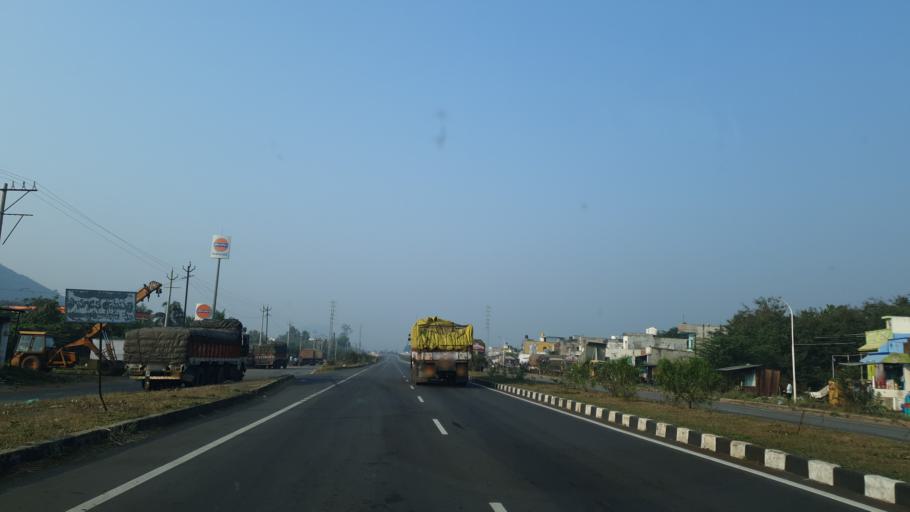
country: IN
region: Andhra Pradesh
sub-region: Srikakulam
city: Tekkali
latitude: 18.5221
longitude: 84.1512
